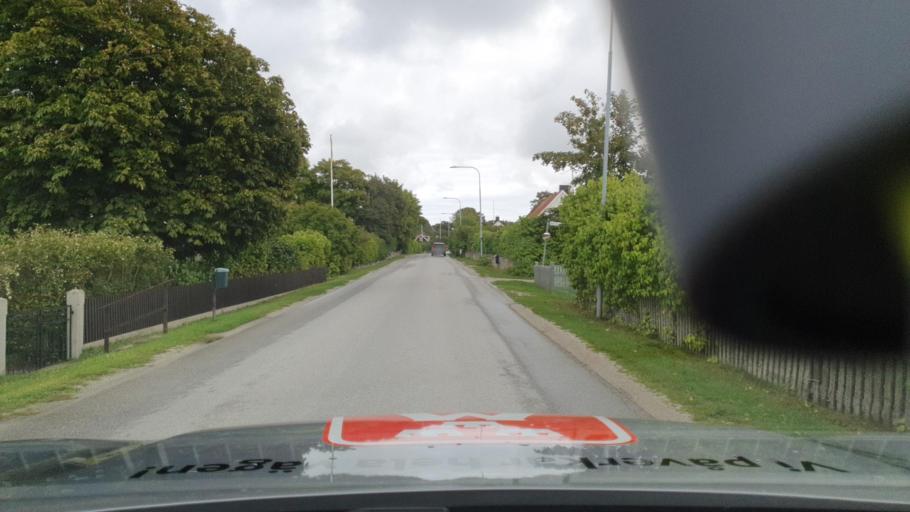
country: SE
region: Gotland
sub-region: Gotland
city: Hemse
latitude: 57.0321
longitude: 18.2635
